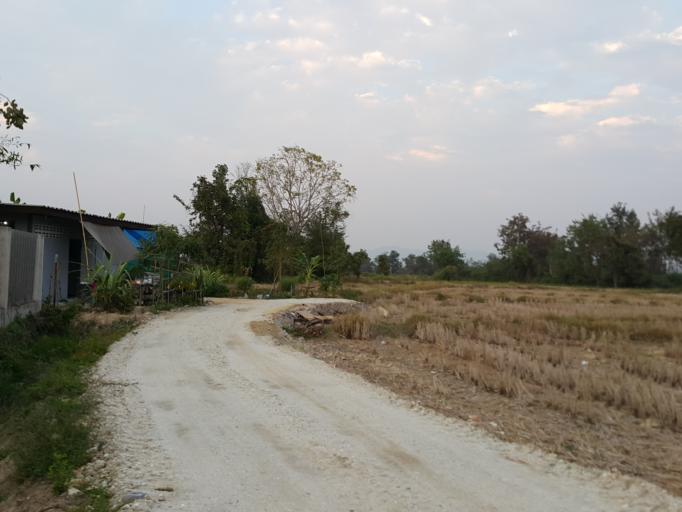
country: TH
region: Chiang Mai
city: San Sai
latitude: 18.8416
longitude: 99.1085
